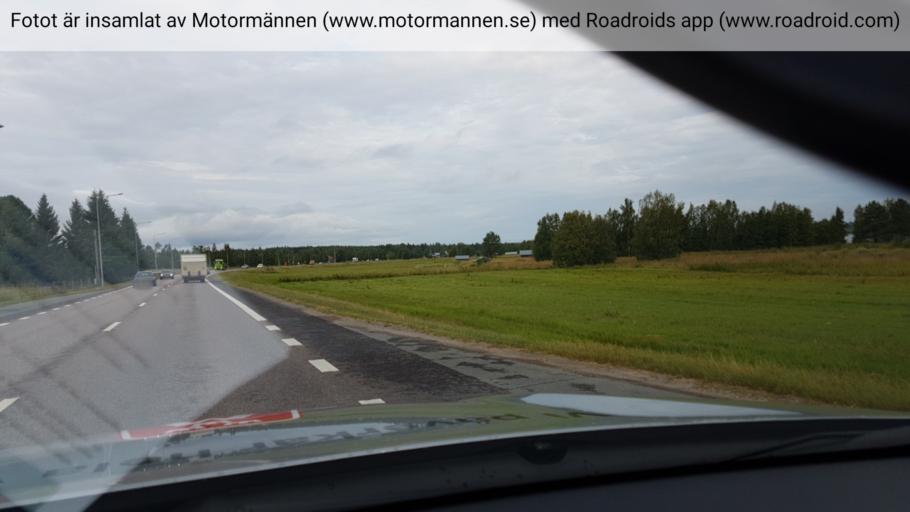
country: SE
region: Norrbotten
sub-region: Lulea Kommun
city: Bergnaset
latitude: 65.5817
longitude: 22.0510
